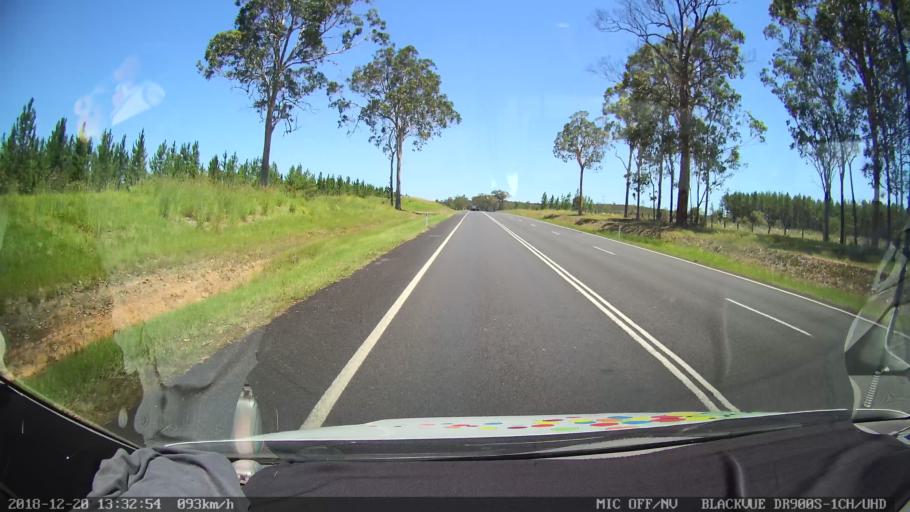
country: AU
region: New South Wales
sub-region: Clarence Valley
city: Gordon
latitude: -29.2382
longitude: 152.9886
